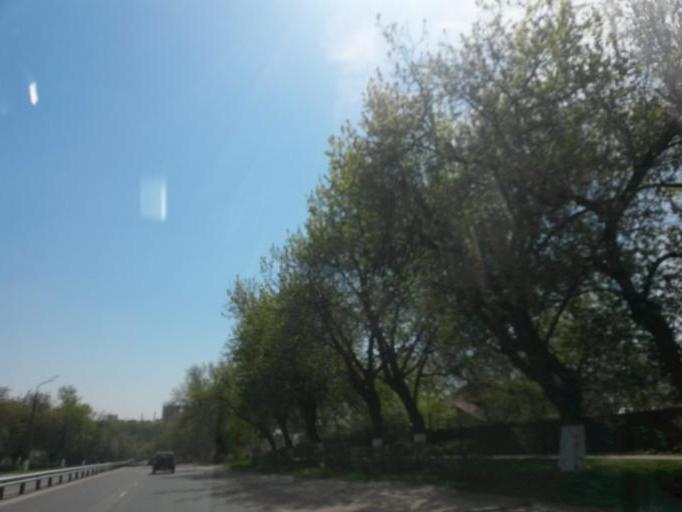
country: RU
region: Moskovskaya
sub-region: Podol'skiy Rayon
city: Podol'sk
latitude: 55.4442
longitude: 37.5520
